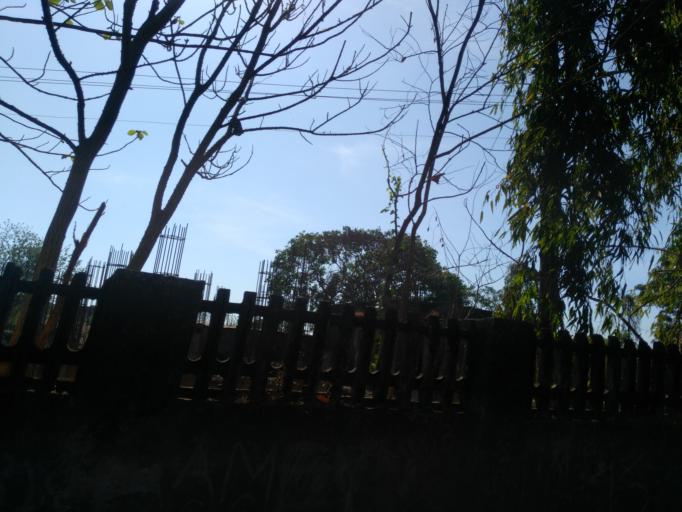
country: IN
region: Maharashtra
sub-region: Ratnagiri
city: Ratnagiri
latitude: 16.9842
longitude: 73.3098
